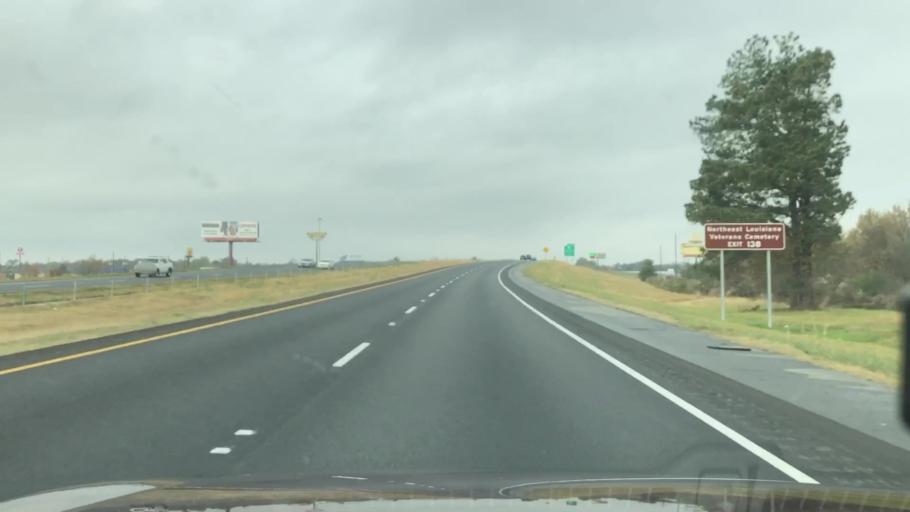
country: US
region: Louisiana
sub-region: Richland Parish
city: Rayville
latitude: 32.4567
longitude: -91.7542
